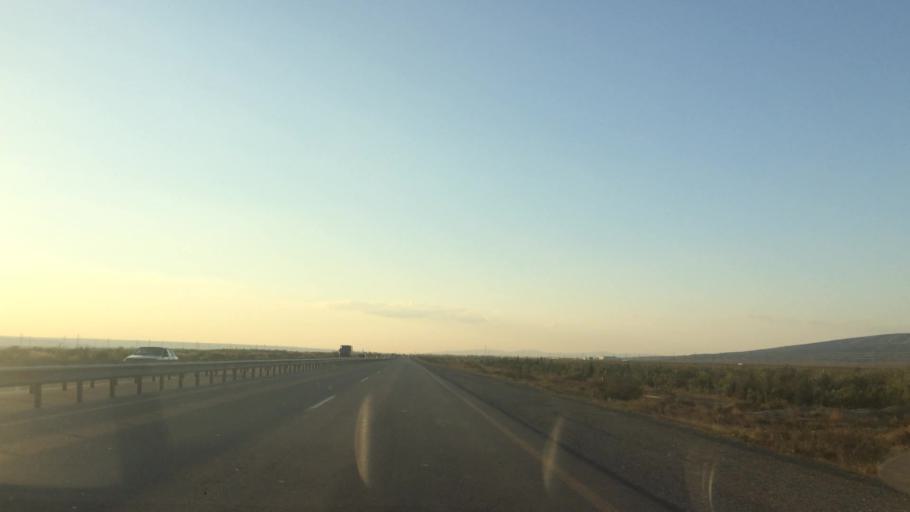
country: AZ
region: Baki
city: Qobustan
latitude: 39.9538
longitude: 49.3154
